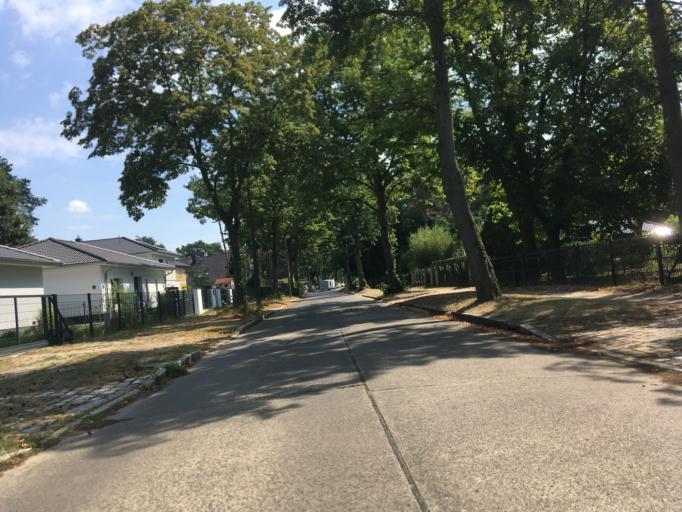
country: DE
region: Berlin
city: Mahlsdorf
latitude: 52.4884
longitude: 13.6123
